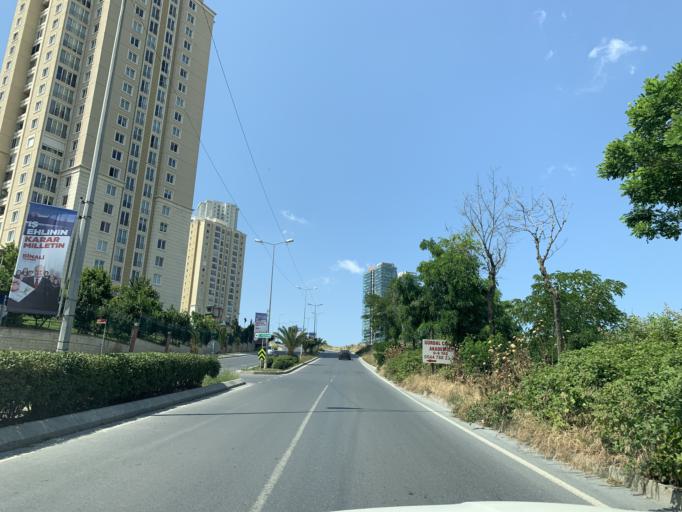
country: TR
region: Istanbul
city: Esenyurt
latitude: 41.0706
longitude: 28.7002
